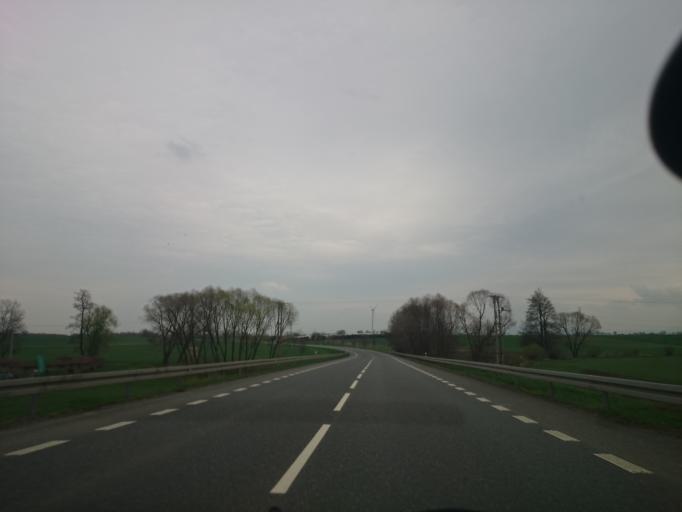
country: PL
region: Opole Voivodeship
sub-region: Powiat nyski
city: Paczkow
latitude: 50.4561
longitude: 16.9856
